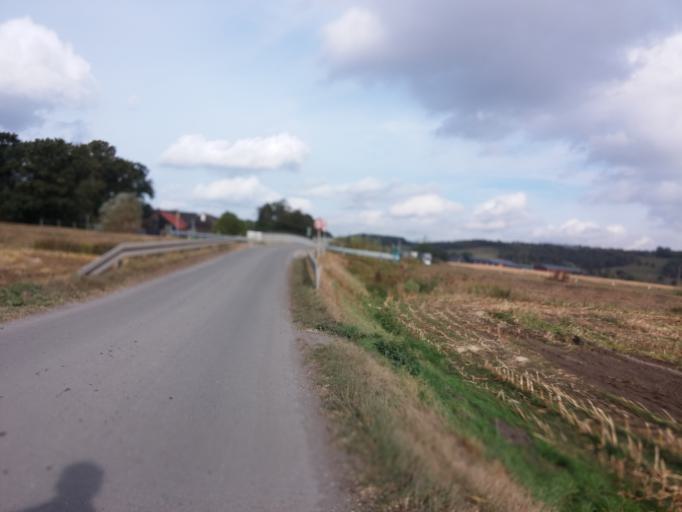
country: DE
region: North Rhine-Westphalia
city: Dorsten
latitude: 51.6450
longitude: 7.0111
